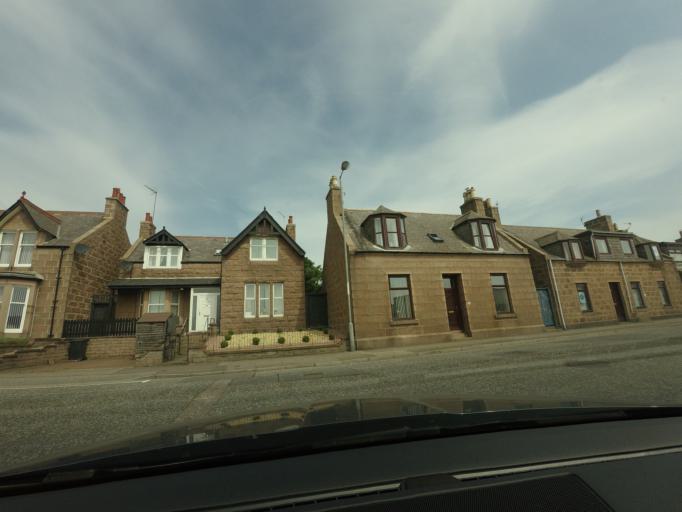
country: GB
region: Scotland
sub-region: Aberdeenshire
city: Peterhead
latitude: 57.5054
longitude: -1.7903
